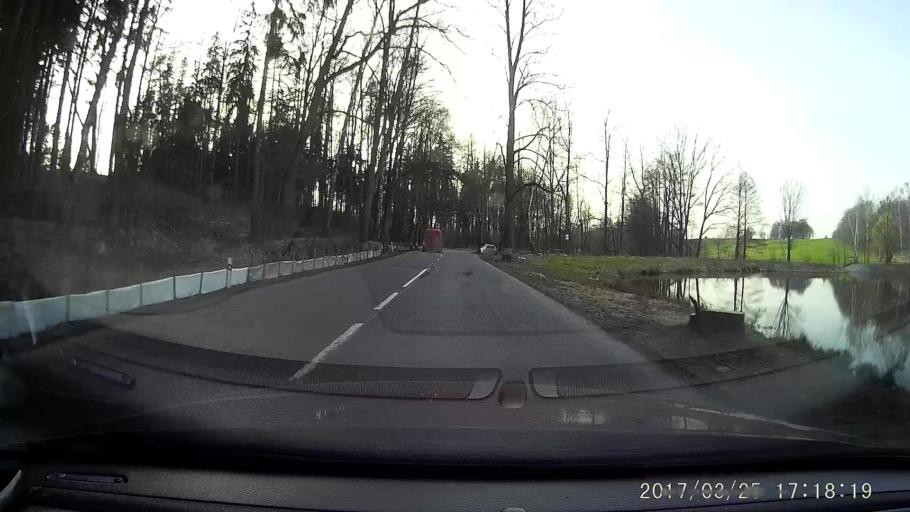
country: CZ
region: Liberecky
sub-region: Okres Liberec
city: Frydlant
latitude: 50.9746
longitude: 15.0850
